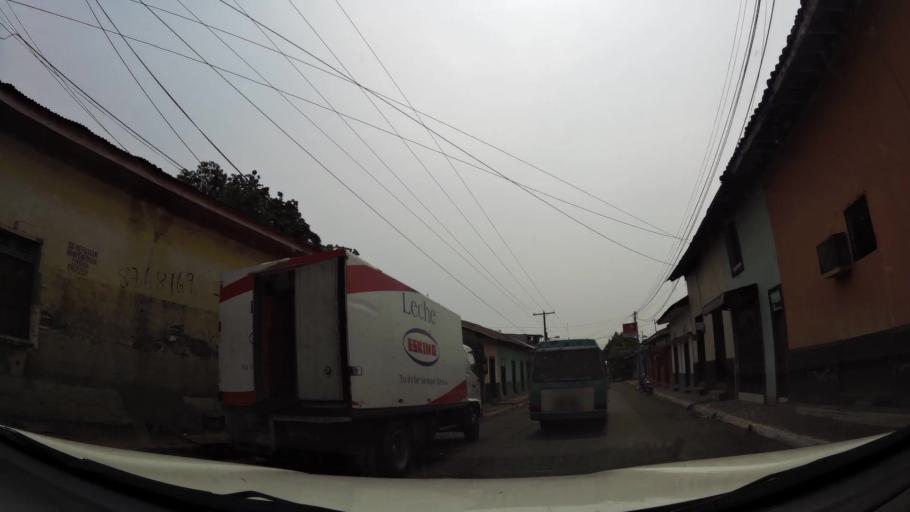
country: NI
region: Chinandega
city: Chinandega
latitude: 12.6334
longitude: -87.1293
